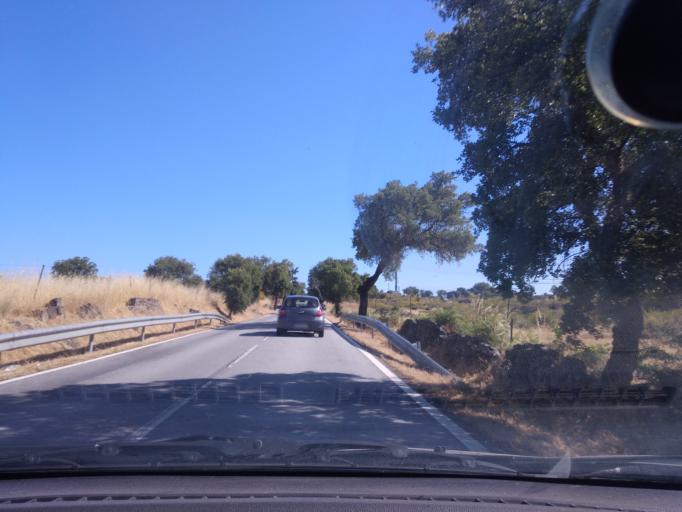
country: PT
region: Portalegre
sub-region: Nisa
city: Nisa
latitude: 39.5004
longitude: -7.6434
